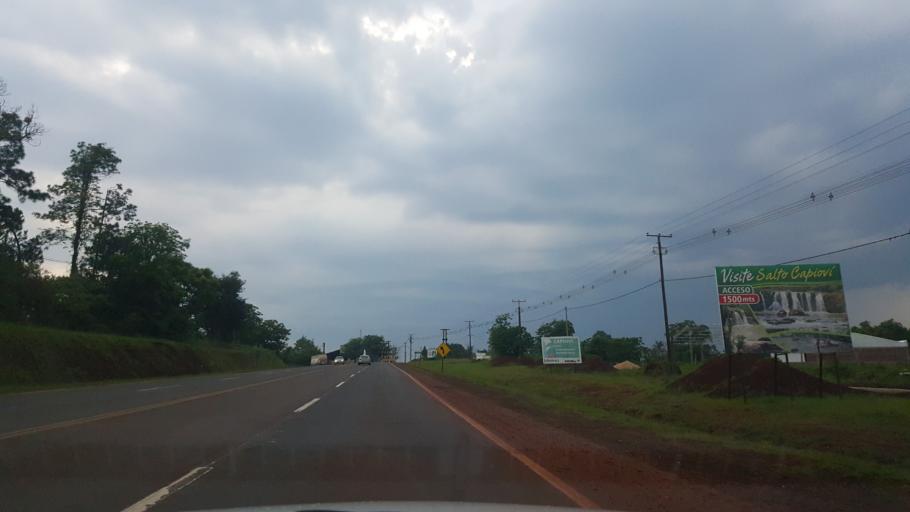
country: AR
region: Misiones
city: Capiovi
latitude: -26.9354
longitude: -55.0645
